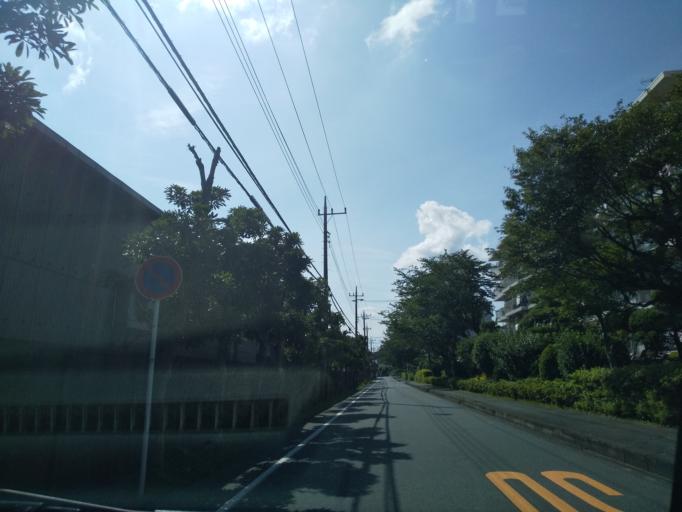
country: JP
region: Kanagawa
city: Zama
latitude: 35.4613
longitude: 139.4129
